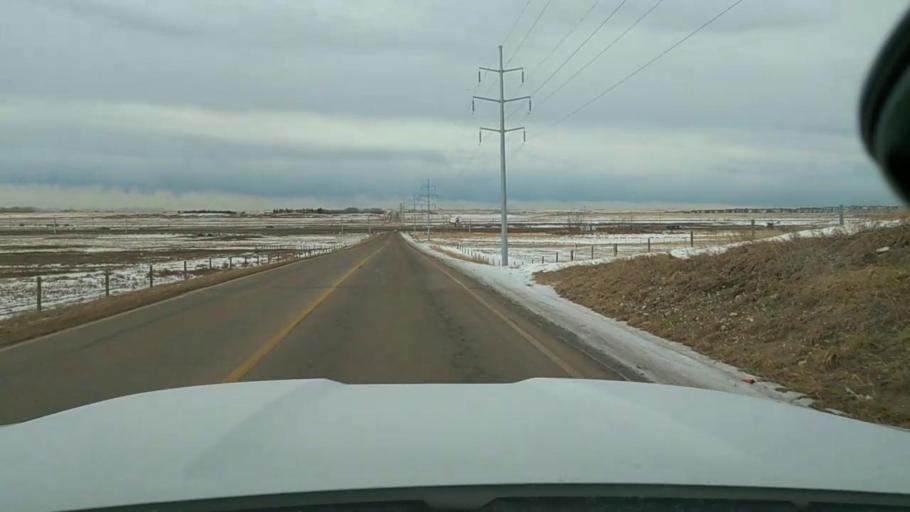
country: CA
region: Alberta
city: Airdrie
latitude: 51.2417
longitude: -113.9936
